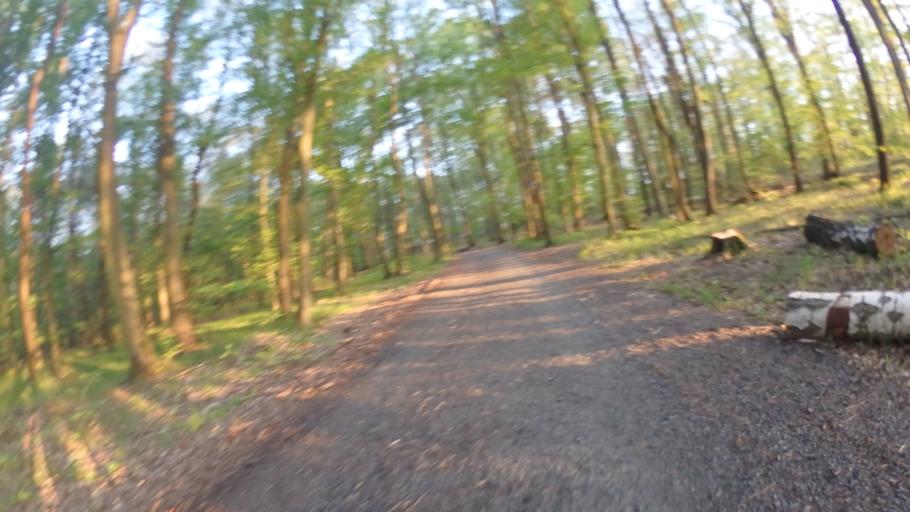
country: CZ
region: South Moravian
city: Troubsko
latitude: 49.1953
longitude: 16.5123
